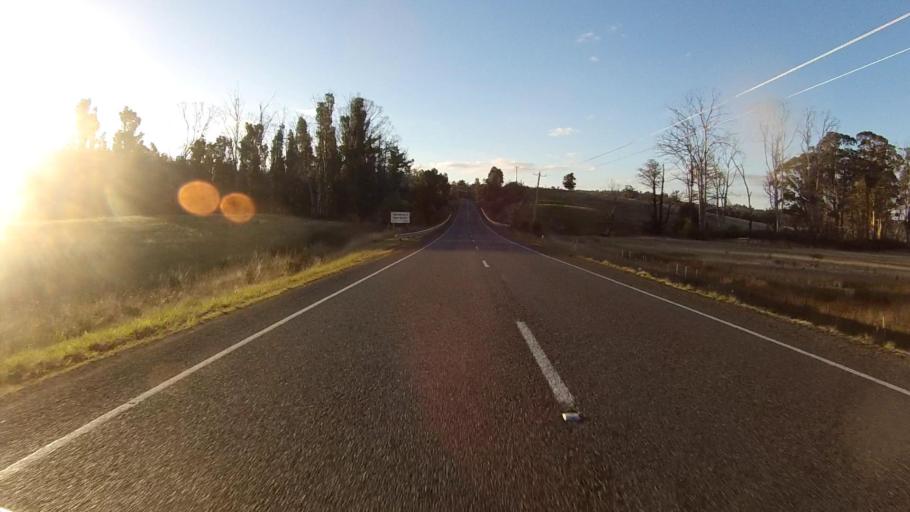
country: AU
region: Tasmania
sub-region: Sorell
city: Sorell
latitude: -42.8635
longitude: 147.8227
